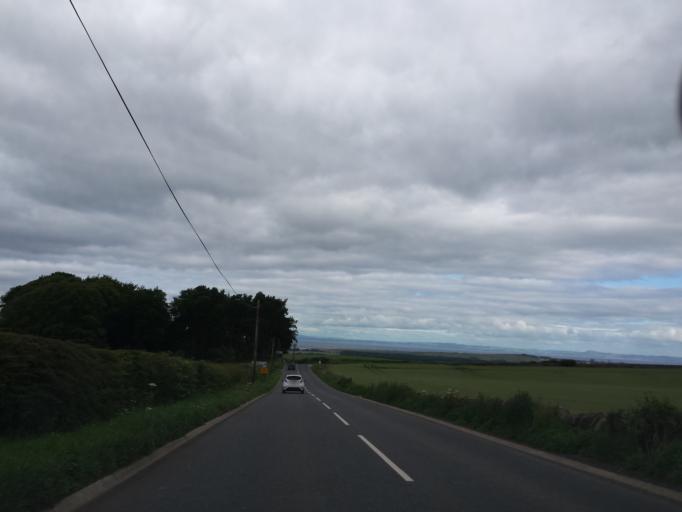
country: GB
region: Scotland
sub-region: East Lothian
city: Haddington
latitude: 55.9750
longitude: -2.8052
